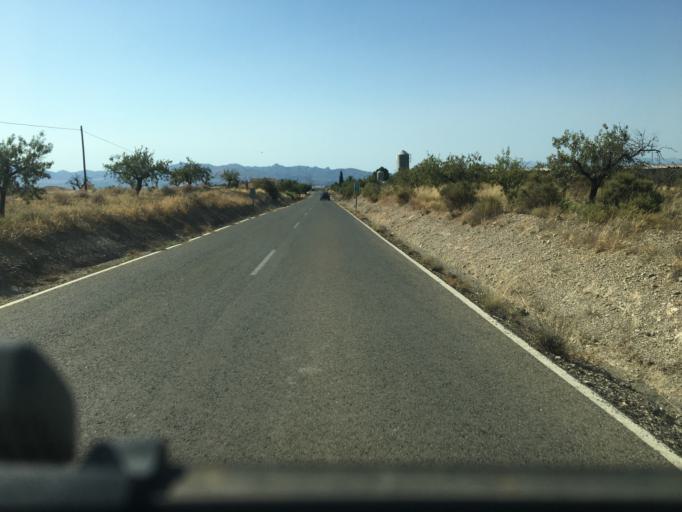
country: ES
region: Andalusia
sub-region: Provincia de Almeria
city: Huercal-Overa
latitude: 37.4520
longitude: -1.9873
